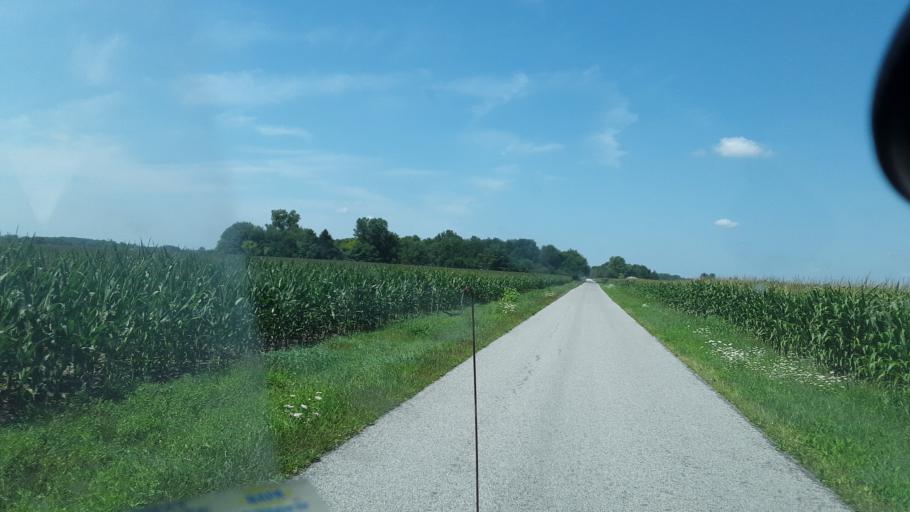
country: US
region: Ohio
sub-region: Hancock County
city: Findlay
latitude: 40.9922
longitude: -83.5193
